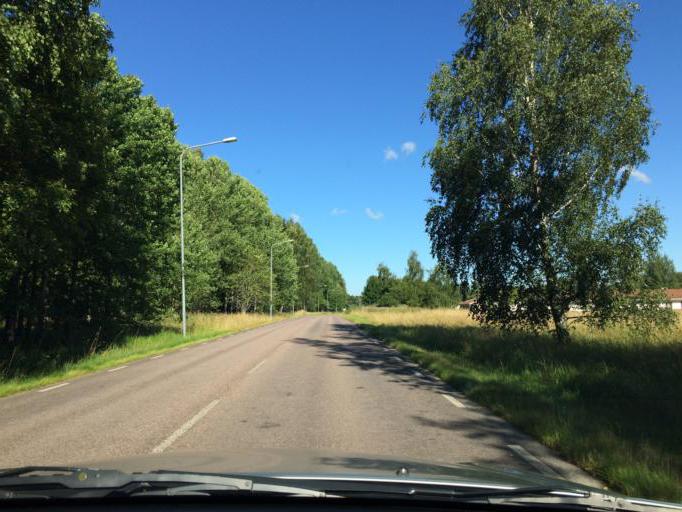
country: SE
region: Vaestmanland
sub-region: Vasteras
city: Vasteras
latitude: 59.5854
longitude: 16.6167
